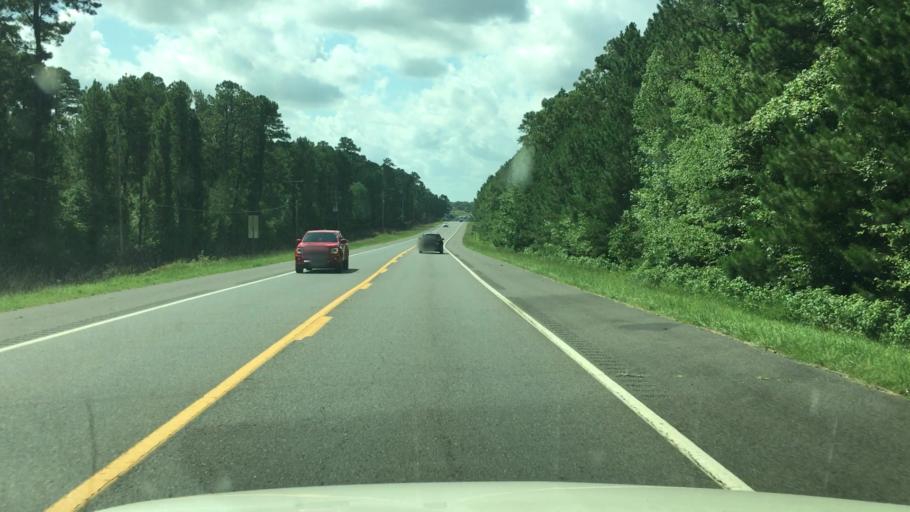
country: US
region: Arkansas
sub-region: Clark County
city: Arkadelphia
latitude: 34.1958
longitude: -93.0754
